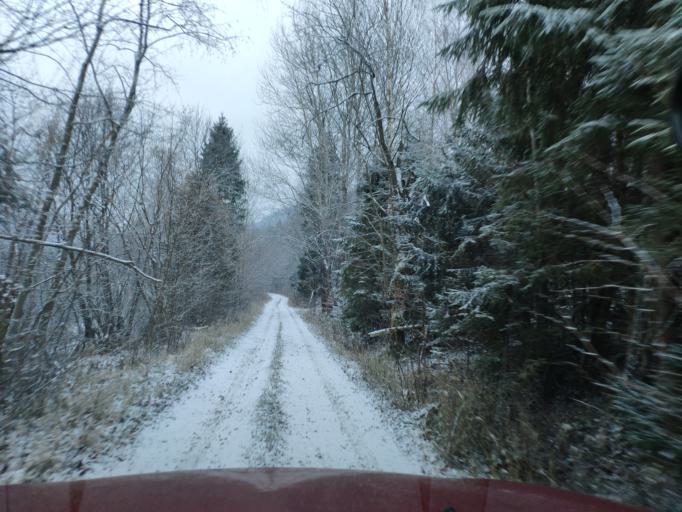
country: SK
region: Kosicky
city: Spisska Nova Ves
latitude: 48.8101
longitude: 20.5243
